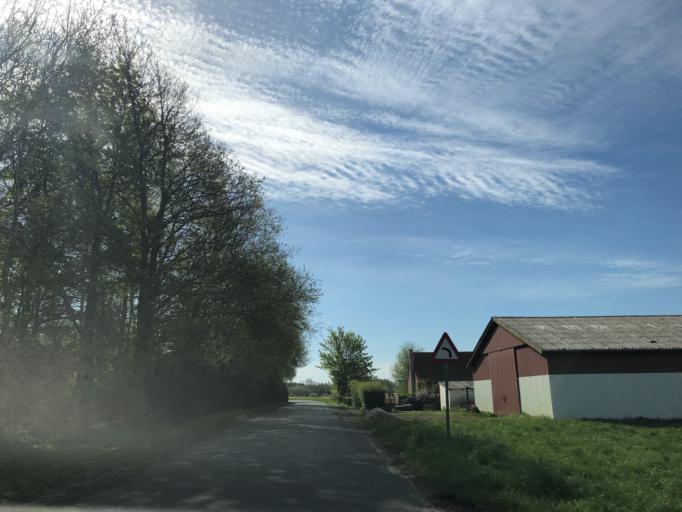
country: DK
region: Zealand
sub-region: Slagelse Kommune
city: Forlev
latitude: 55.3812
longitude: 11.2925
